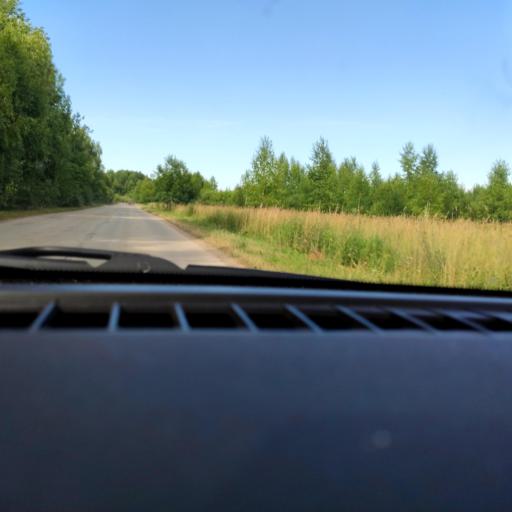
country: RU
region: Perm
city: Polazna
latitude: 58.3588
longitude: 56.2471
